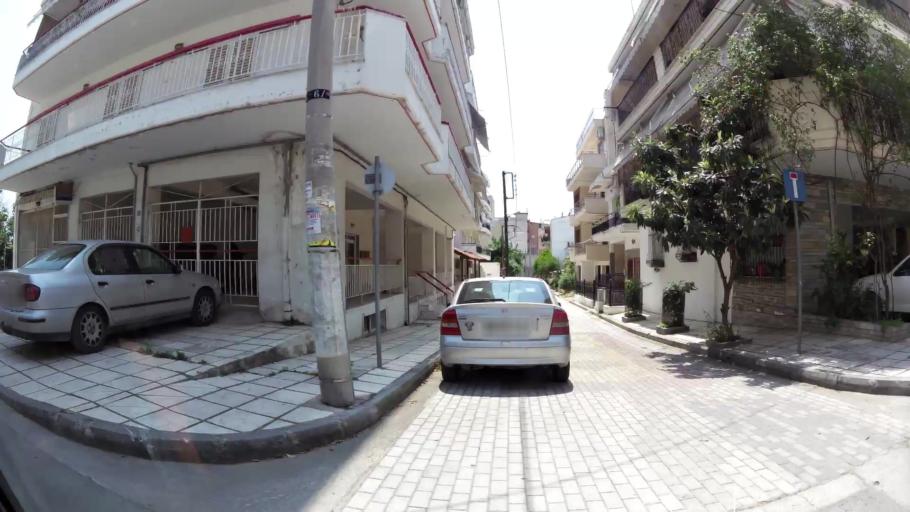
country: GR
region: Central Macedonia
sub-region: Nomos Thessalonikis
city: Evosmos
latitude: 40.6664
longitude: 22.9021
